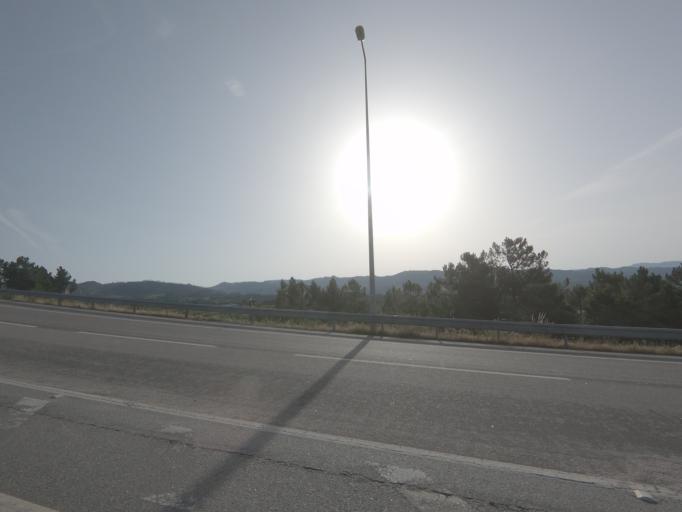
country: PT
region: Vila Real
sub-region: Sabrosa
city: Sabrosa
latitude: 41.2830
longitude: -7.4735
